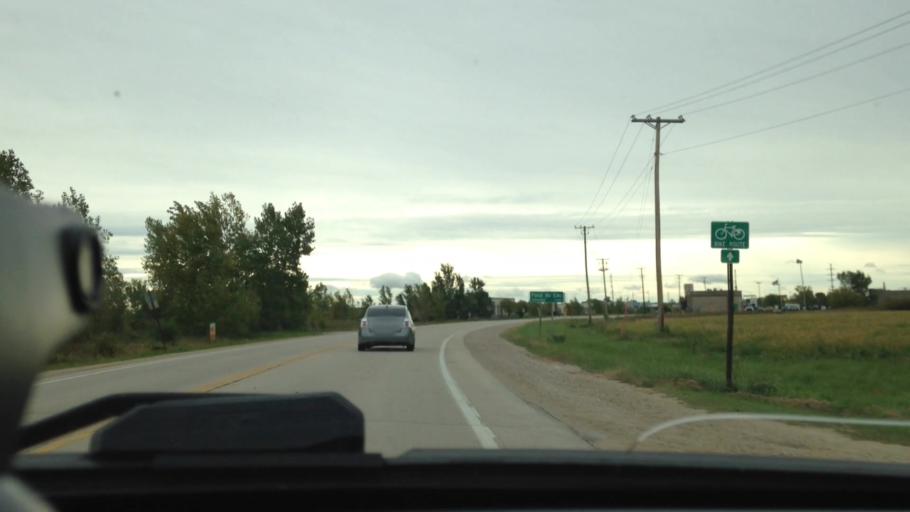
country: US
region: Wisconsin
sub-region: Fond du Lac County
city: North Fond du Lac
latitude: 43.7956
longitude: -88.4876
